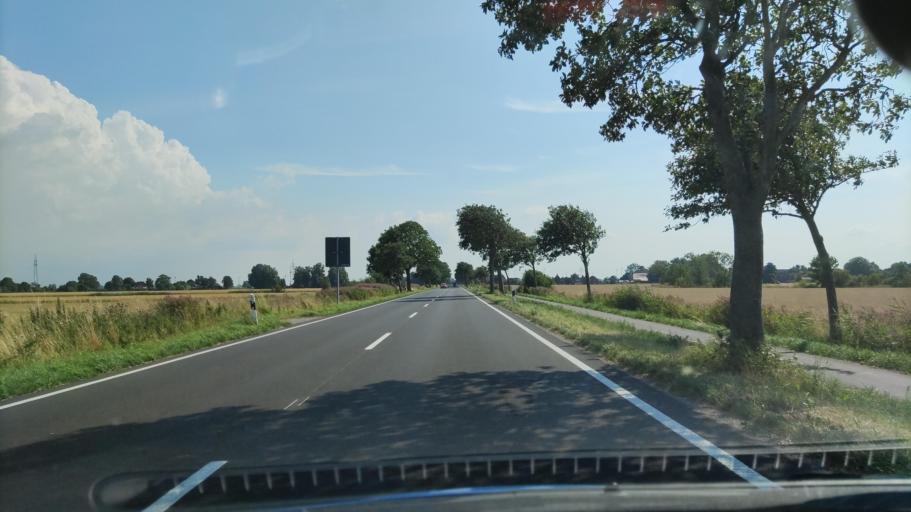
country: DE
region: Lower Saxony
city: Werdum
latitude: 53.6736
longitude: 7.7924
